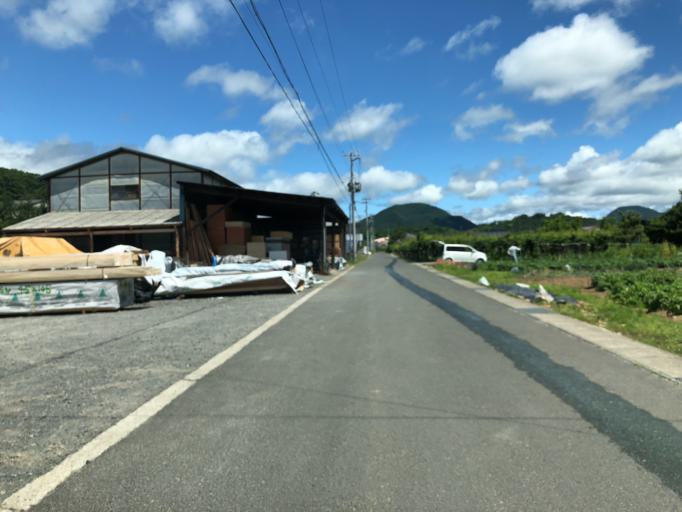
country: JP
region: Fukushima
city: Fukushima-shi
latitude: 37.8150
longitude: 140.4246
